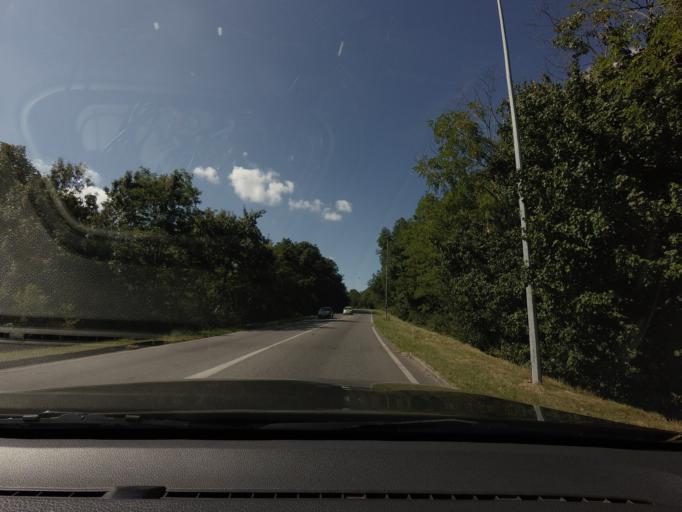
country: FR
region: Midi-Pyrenees
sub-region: Departement de la Haute-Garonne
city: Cornebarrieu
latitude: 43.6465
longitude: 1.3359
